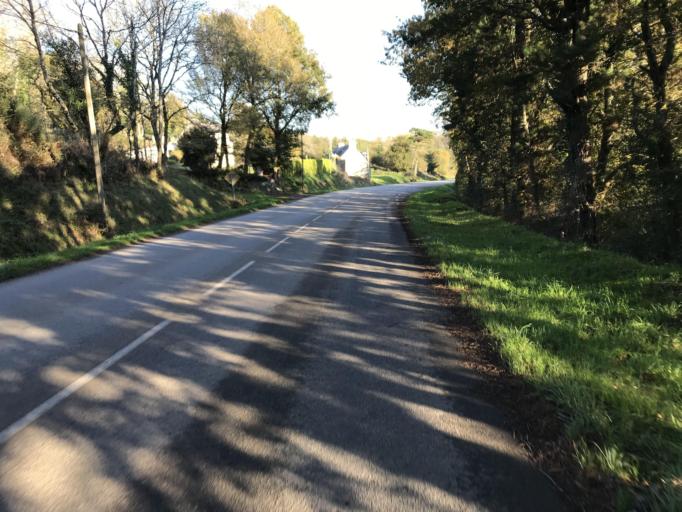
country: FR
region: Brittany
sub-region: Departement du Finistere
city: Hopital-Camfrout
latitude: 48.3146
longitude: -4.2219
